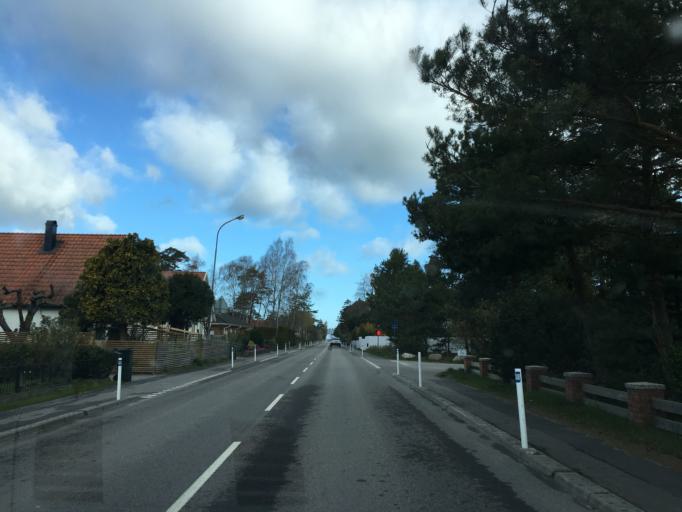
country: SE
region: Skane
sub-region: Vellinge Kommun
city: Hollviken
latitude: 55.4126
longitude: 12.9555
